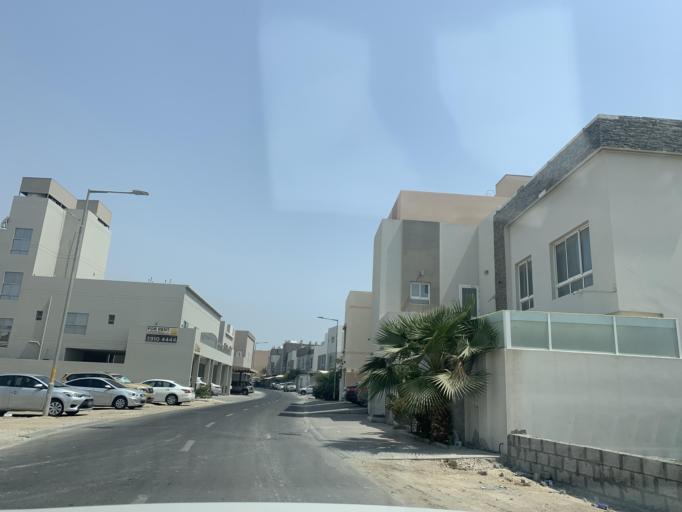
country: BH
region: Manama
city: Jidd Hafs
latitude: 26.2081
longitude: 50.5030
